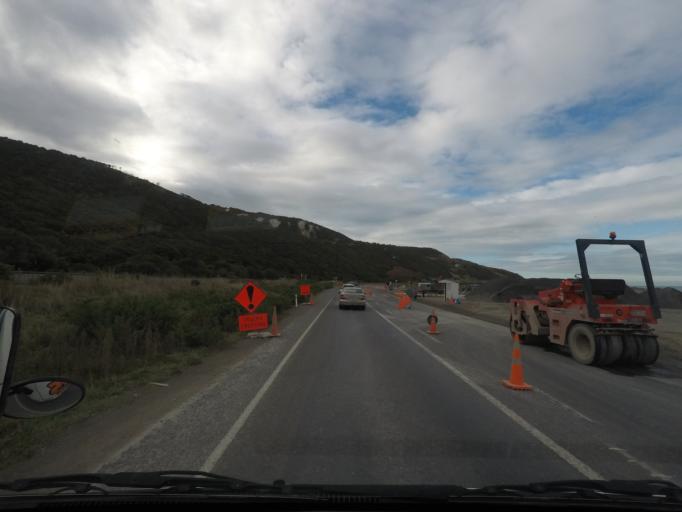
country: NZ
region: Canterbury
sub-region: Kaikoura District
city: Kaikoura
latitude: -42.2179
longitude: 173.8586
